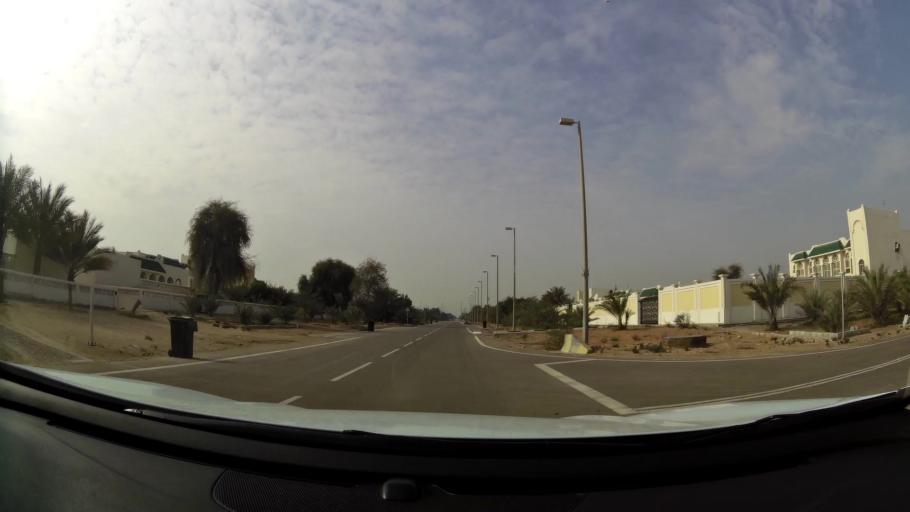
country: AE
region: Abu Dhabi
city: Abu Dhabi
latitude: 24.6646
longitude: 54.7644
